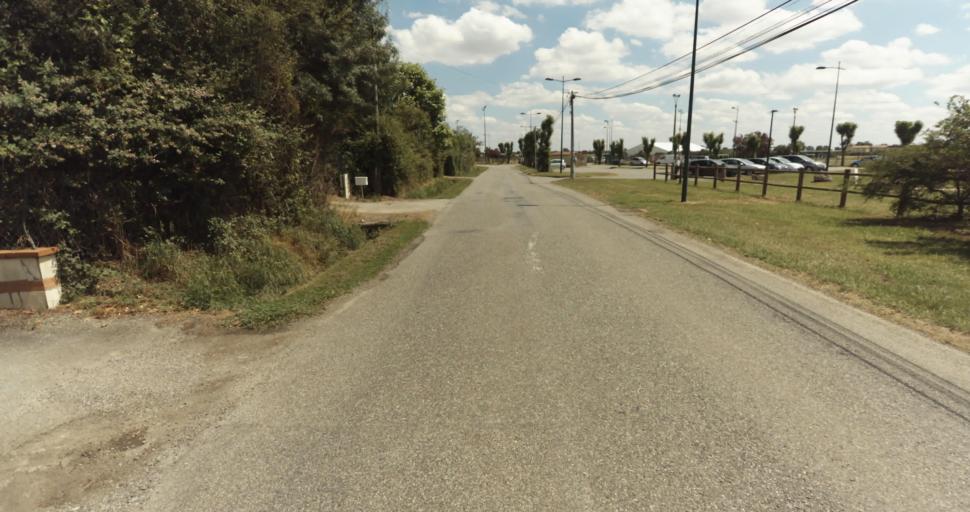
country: FR
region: Midi-Pyrenees
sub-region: Departement de la Haute-Garonne
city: Fontenilles
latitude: 43.5580
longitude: 1.1770
